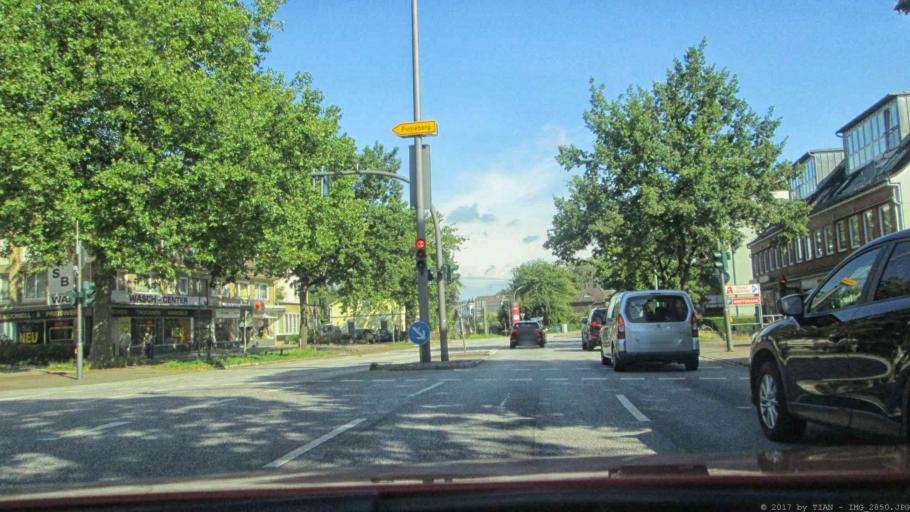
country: DE
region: Hamburg
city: Eidelstedt
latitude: 53.6087
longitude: 9.9050
